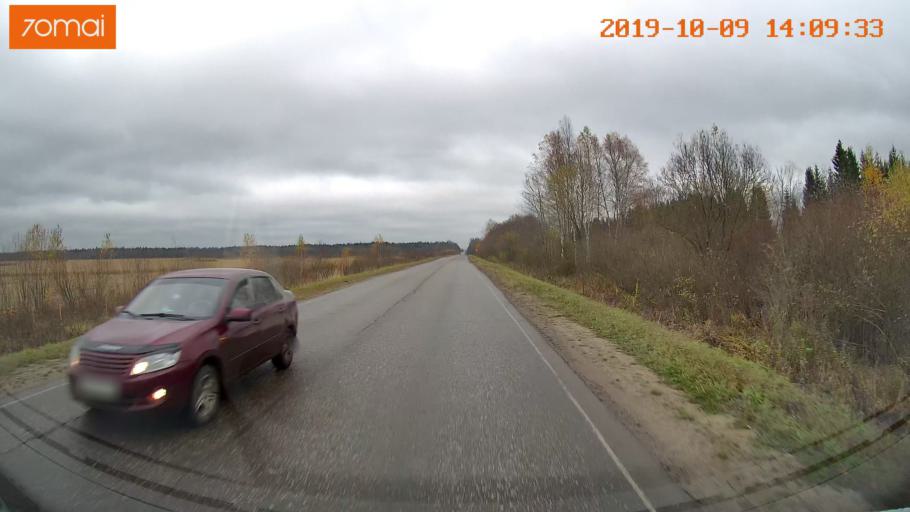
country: RU
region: Kostroma
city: Buy
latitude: 58.4810
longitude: 41.4546
